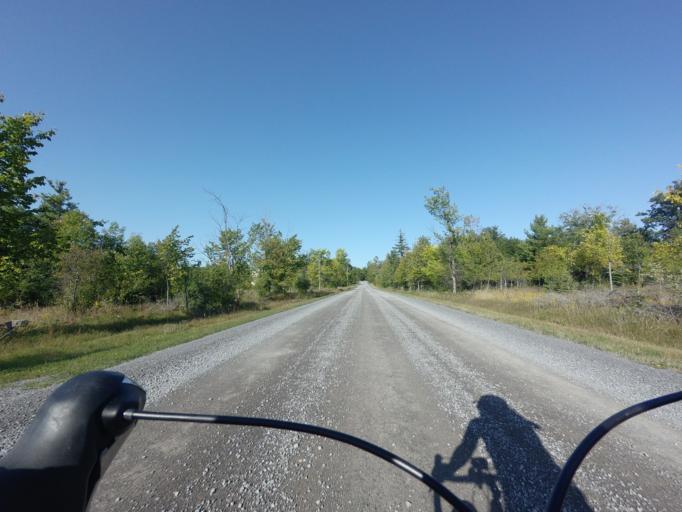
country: CA
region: Ontario
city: Bells Corners
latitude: 45.4841
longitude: -76.0394
